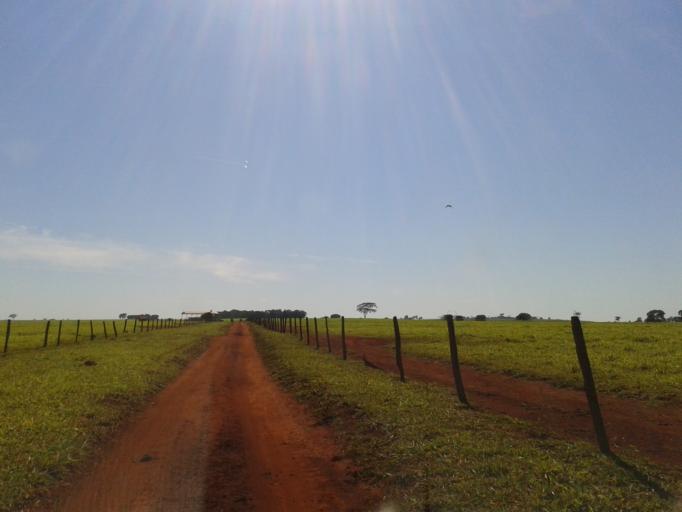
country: BR
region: Minas Gerais
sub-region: Centralina
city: Centralina
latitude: -18.6520
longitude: -49.2911
